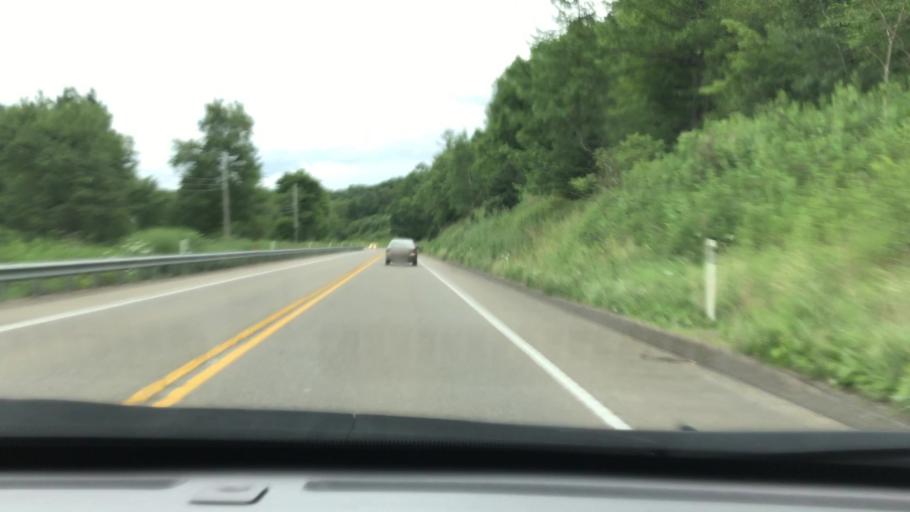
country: US
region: Pennsylvania
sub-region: Elk County
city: Johnsonburg
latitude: 41.5380
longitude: -78.6826
